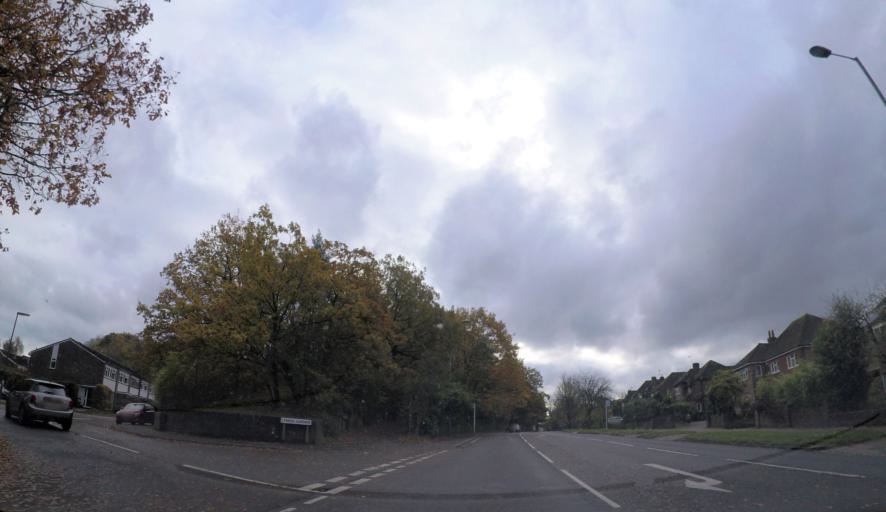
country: GB
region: England
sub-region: Surrey
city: Reigate
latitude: 51.2317
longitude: -0.2028
